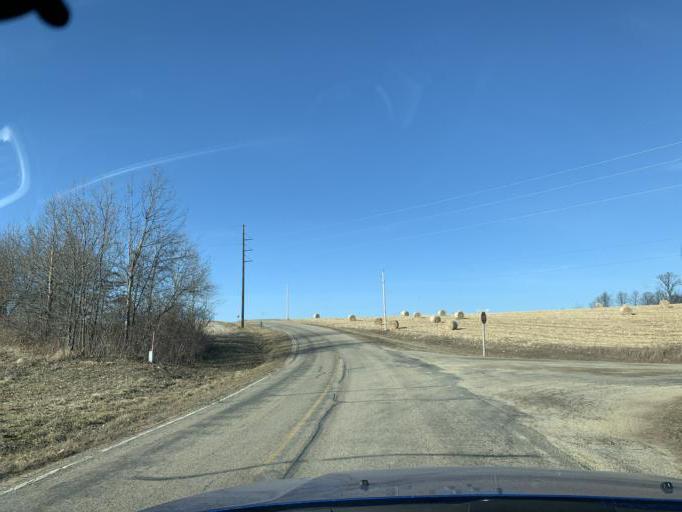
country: US
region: Wisconsin
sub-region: Iowa County
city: Barneveld
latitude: 42.8570
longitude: -89.9364
